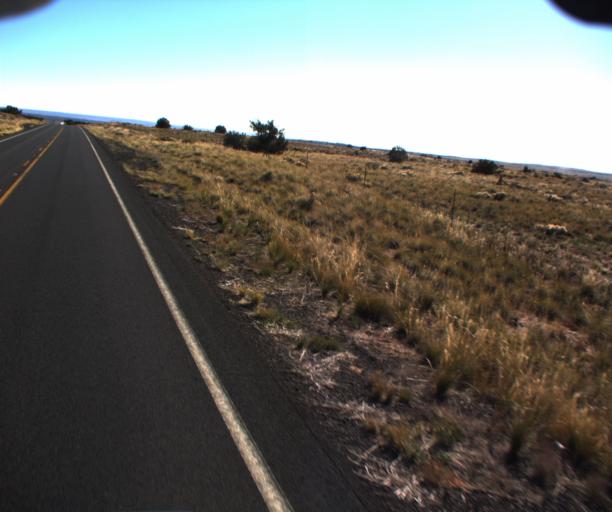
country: US
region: Arizona
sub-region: Apache County
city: Houck
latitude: 35.2404
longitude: -109.4393
